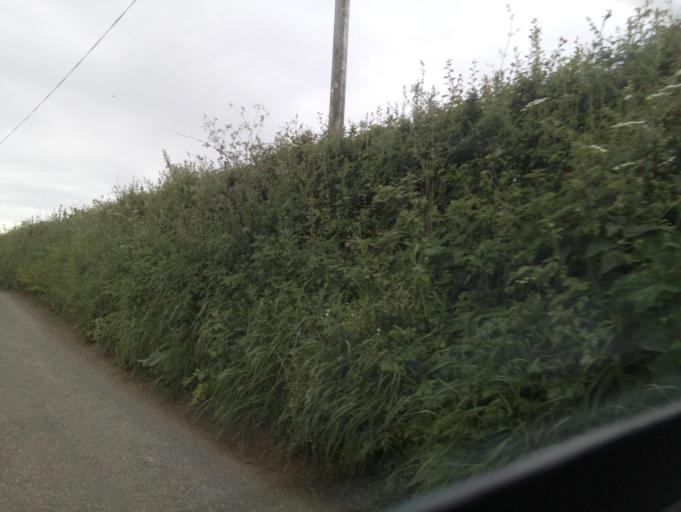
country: GB
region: England
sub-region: Devon
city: Dartmouth
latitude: 50.3188
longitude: -3.6347
